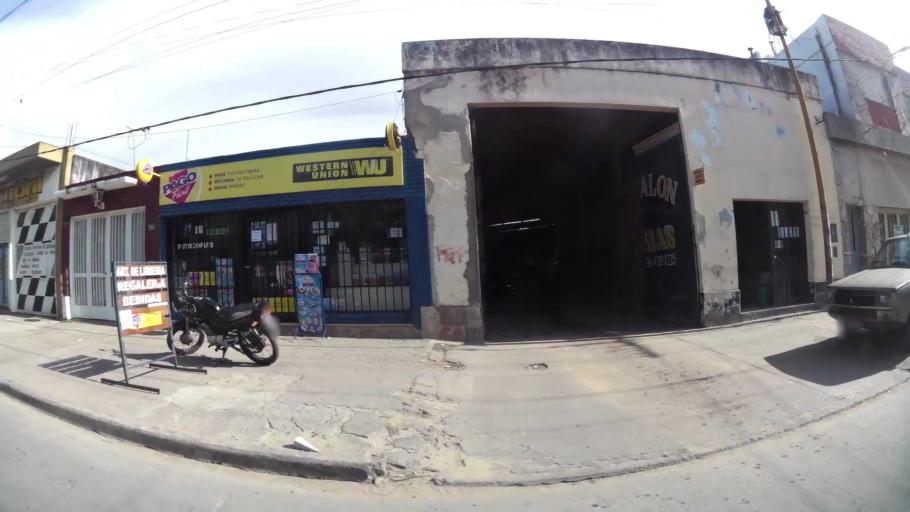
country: AR
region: Santa Fe
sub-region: Departamento de Rosario
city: Rosario
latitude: -32.9273
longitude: -60.6995
